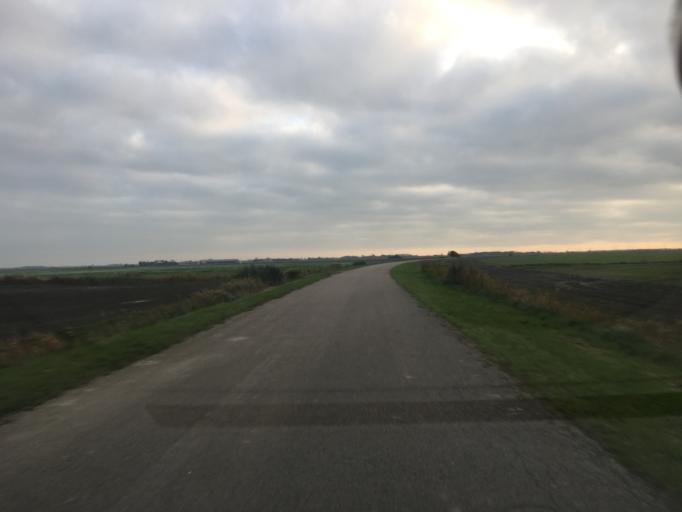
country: DE
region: Schleswig-Holstein
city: Aventoft
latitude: 54.9259
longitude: 8.7720
